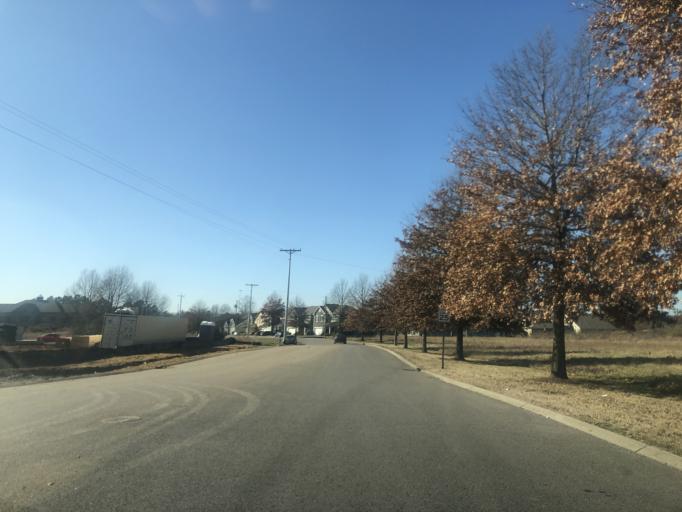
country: US
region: Tennessee
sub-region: Rutherford County
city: Smyrna
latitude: 35.9390
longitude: -86.5294
